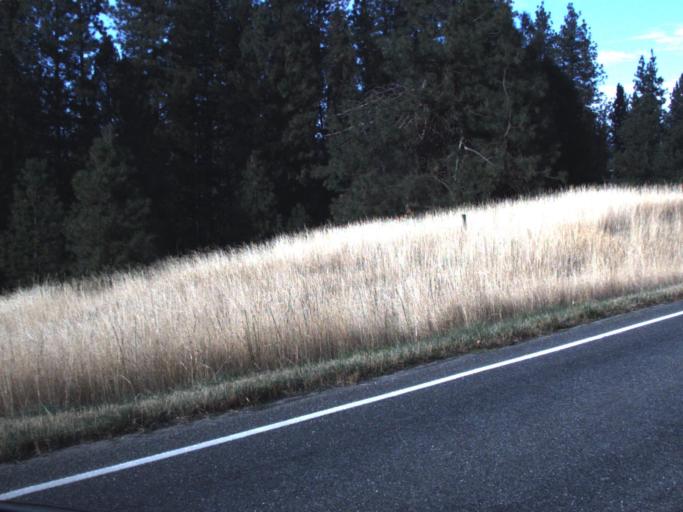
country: US
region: Washington
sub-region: Stevens County
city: Kettle Falls
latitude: 48.5091
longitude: -118.1489
